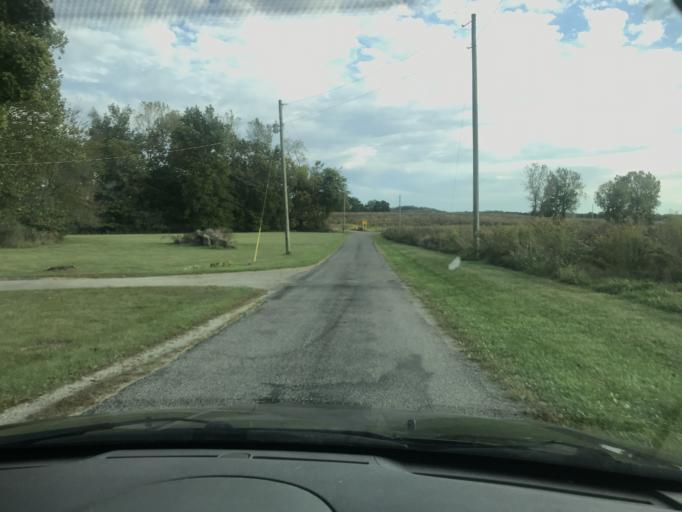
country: US
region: Ohio
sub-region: Logan County
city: West Liberty
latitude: 40.2211
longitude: -83.6753
